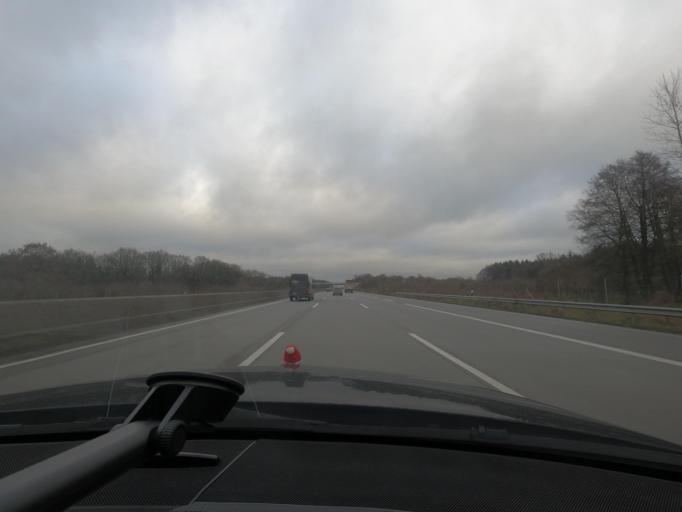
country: DE
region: Schleswig-Holstein
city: Bimohlen
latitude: 53.9253
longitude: 9.9407
